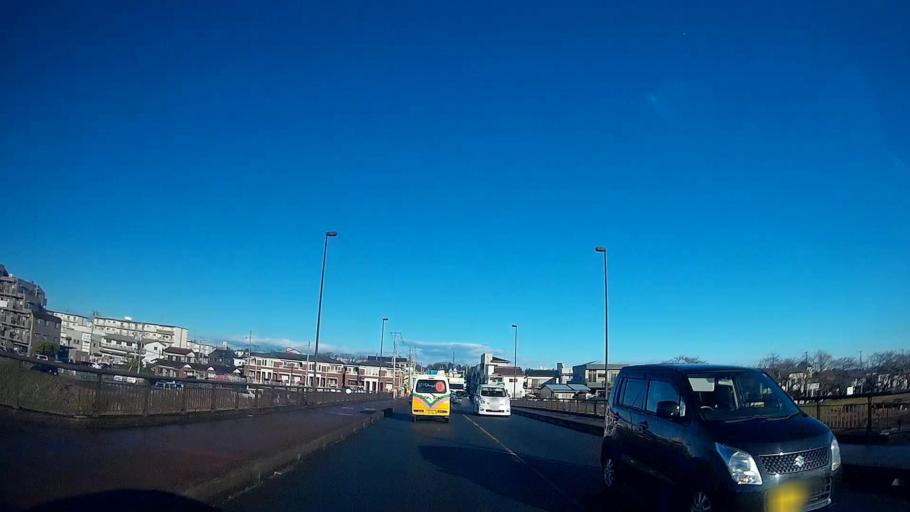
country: JP
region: Saitama
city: Sayama
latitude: 35.8516
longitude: 139.3830
